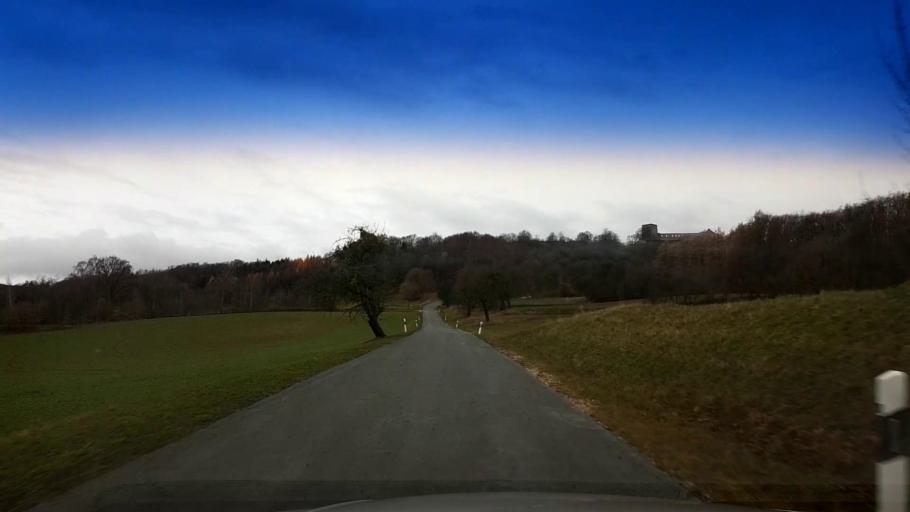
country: DE
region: Bavaria
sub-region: Upper Franconia
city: Schesslitz
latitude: 49.9629
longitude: 11.0519
